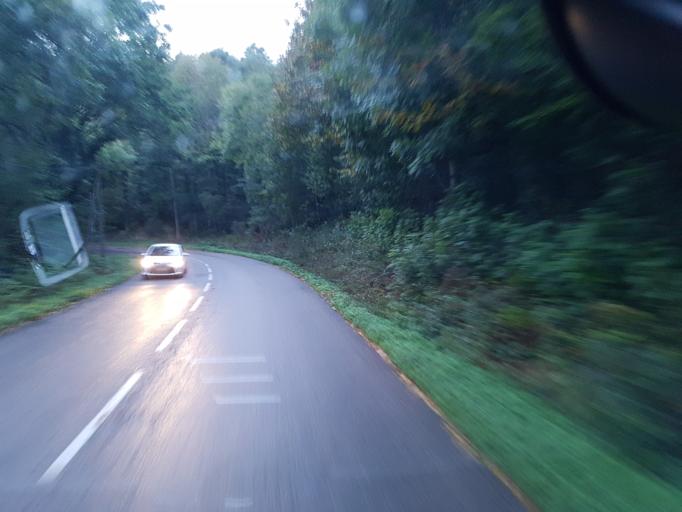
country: FR
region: Midi-Pyrenees
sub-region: Departement du Tarn
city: Mazamet
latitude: 43.4639
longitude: 2.3559
